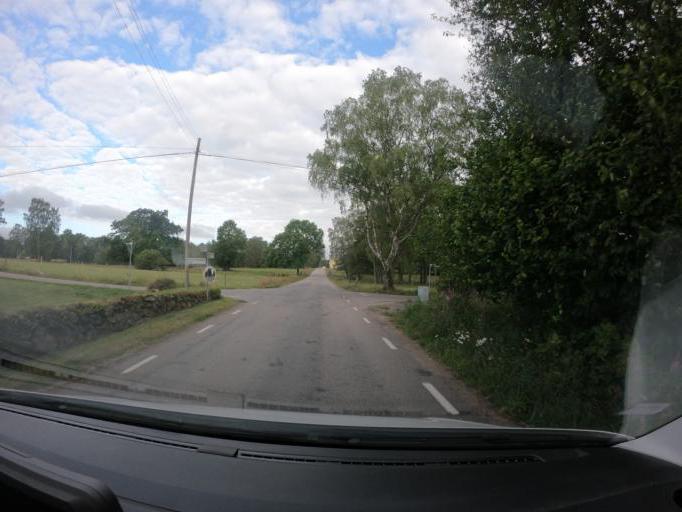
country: SE
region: Skane
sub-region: Angelholms Kommun
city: Munka-Ljungby
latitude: 56.3119
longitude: 13.0264
